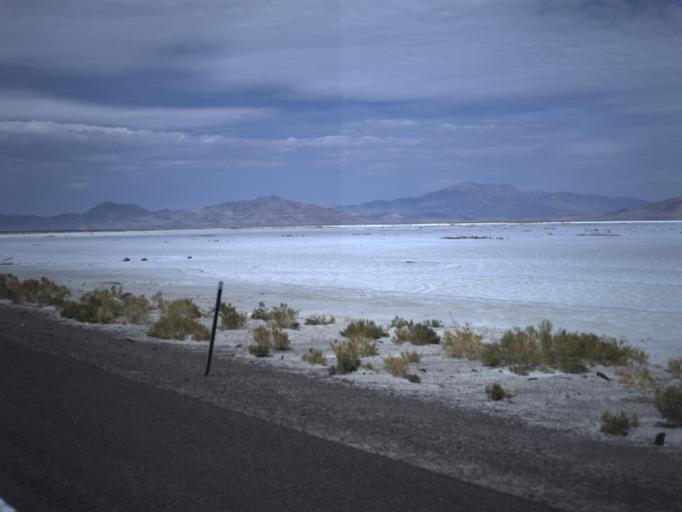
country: US
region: Utah
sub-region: Tooele County
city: Wendover
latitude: 40.7368
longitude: -113.7239
